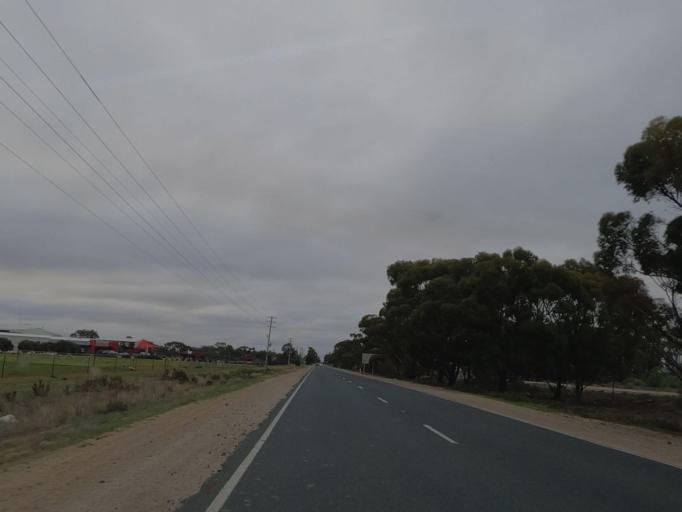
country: AU
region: Victoria
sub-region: Swan Hill
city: Swan Hill
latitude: -35.3897
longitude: 143.5694
